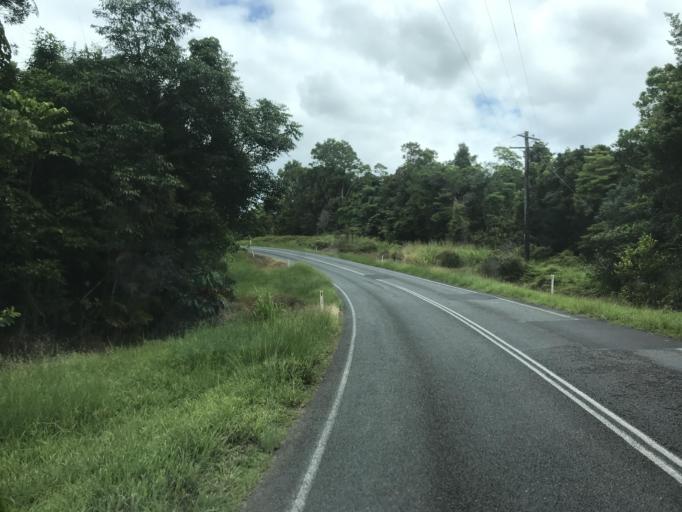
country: AU
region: Queensland
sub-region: Cassowary Coast
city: Innisfail
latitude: -17.8297
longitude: 146.0555
